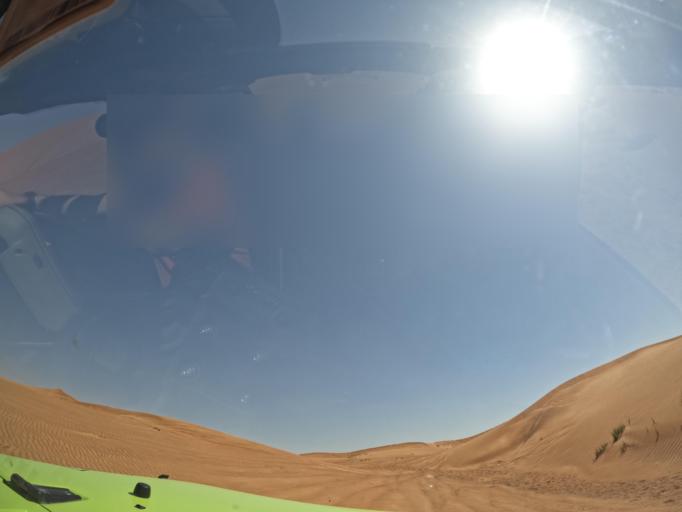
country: AE
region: Ash Shariqah
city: Adh Dhayd
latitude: 25.0071
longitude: 55.7333
